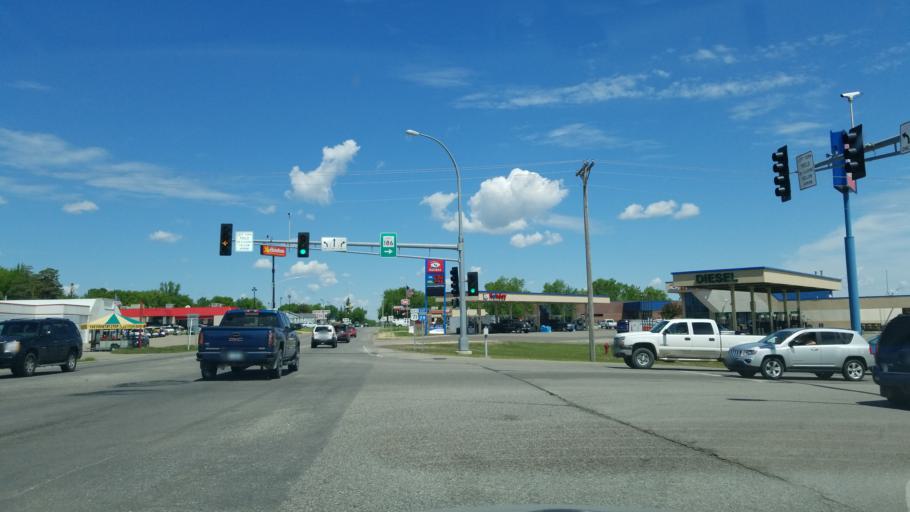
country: US
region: Minnesota
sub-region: Stearns County
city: Sauk Centre
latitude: 45.7230
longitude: -94.9513
